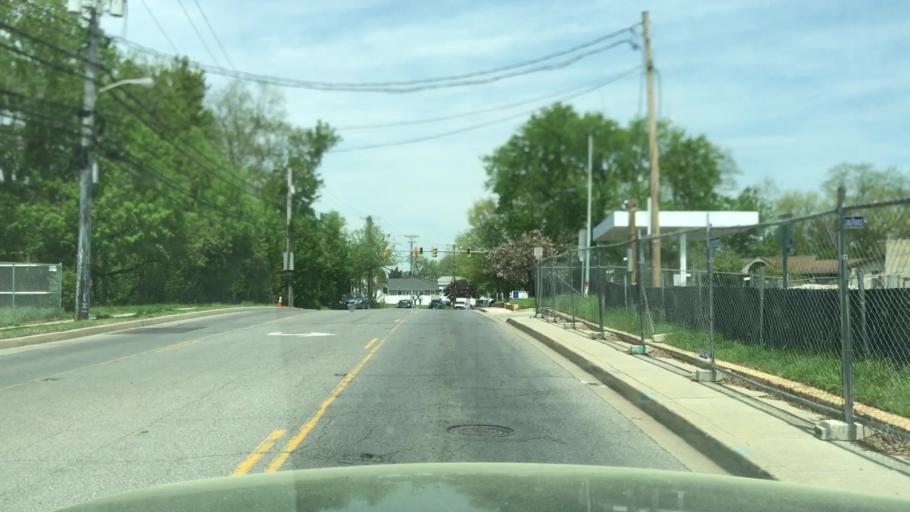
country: US
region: Maryland
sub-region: Anne Arundel County
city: Annapolis
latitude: 38.9725
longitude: -76.5099
